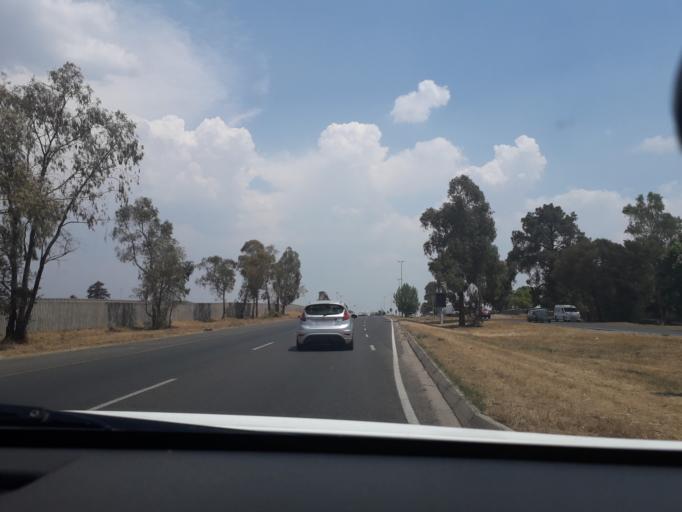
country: ZA
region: Gauteng
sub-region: City of Johannesburg Metropolitan Municipality
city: Midrand
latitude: -25.9795
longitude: 28.1339
